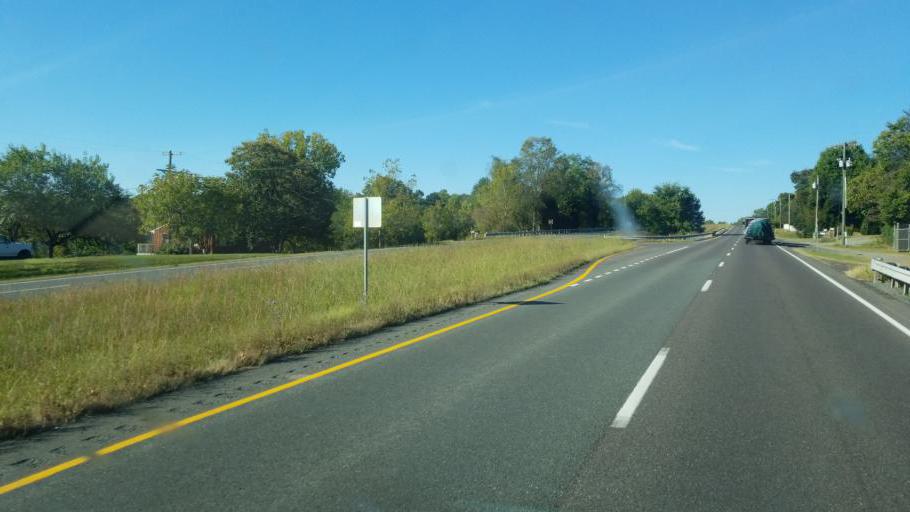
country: US
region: Virginia
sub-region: Madison County
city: Brightwood
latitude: 38.4299
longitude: -78.1687
